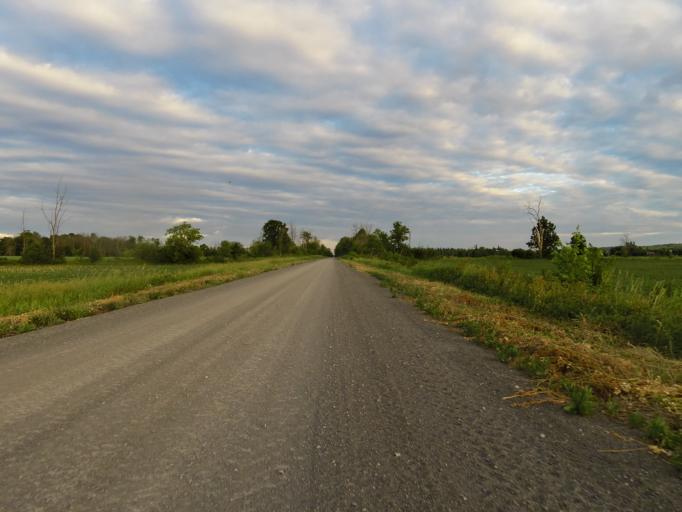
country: CA
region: Ontario
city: Arnprior
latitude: 45.3447
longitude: -76.3003
